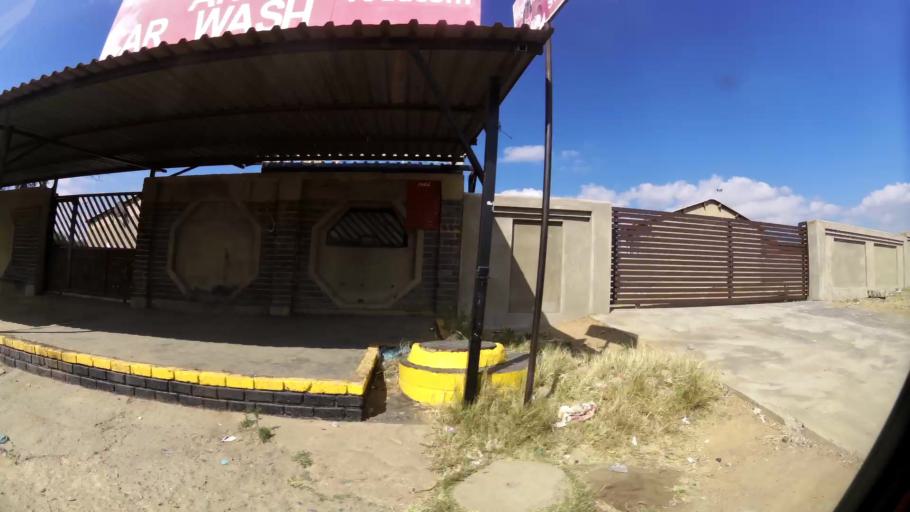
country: ZA
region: Gauteng
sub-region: Ekurhuleni Metropolitan Municipality
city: Tembisa
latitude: -26.0189
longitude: 28.1914
